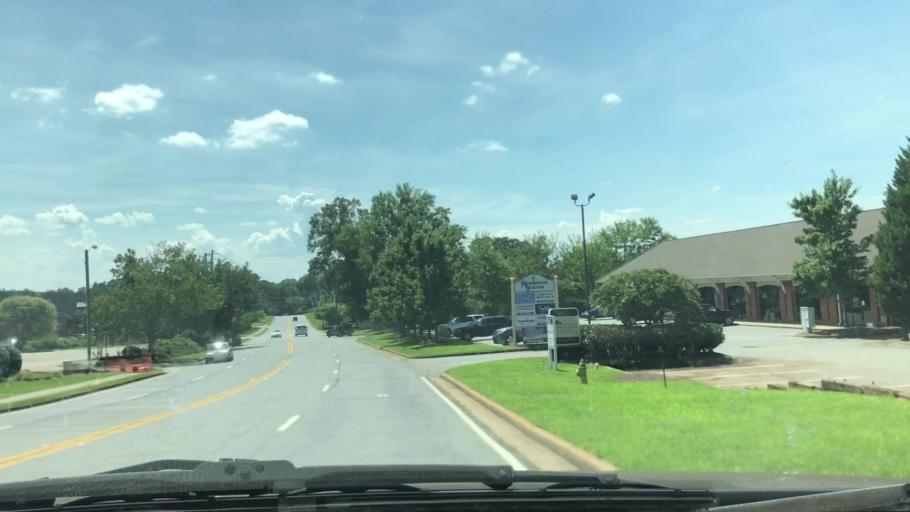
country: US
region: Georgia
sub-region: Bartow County
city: Cartersville
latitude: 34.1929
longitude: -84.7915
